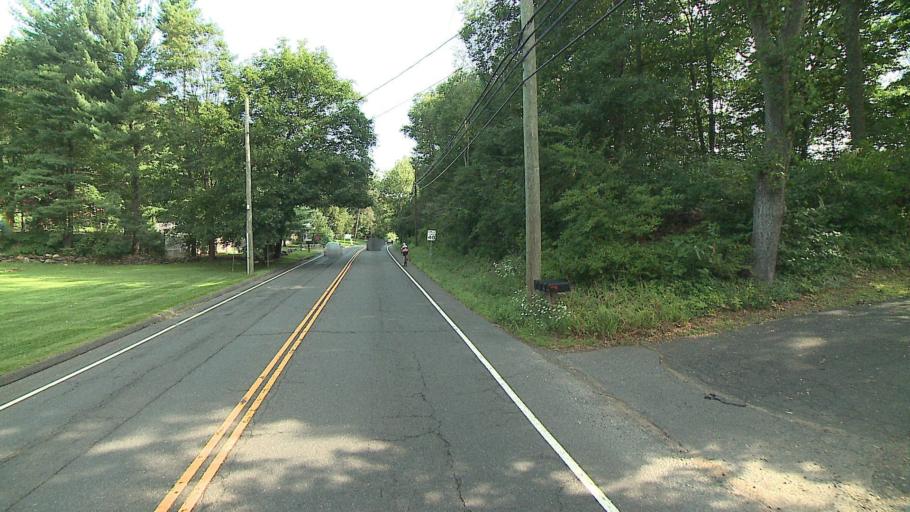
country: US
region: Connecticut
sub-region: Fairfield County
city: Wilton
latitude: 41.2246
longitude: -73.4257
